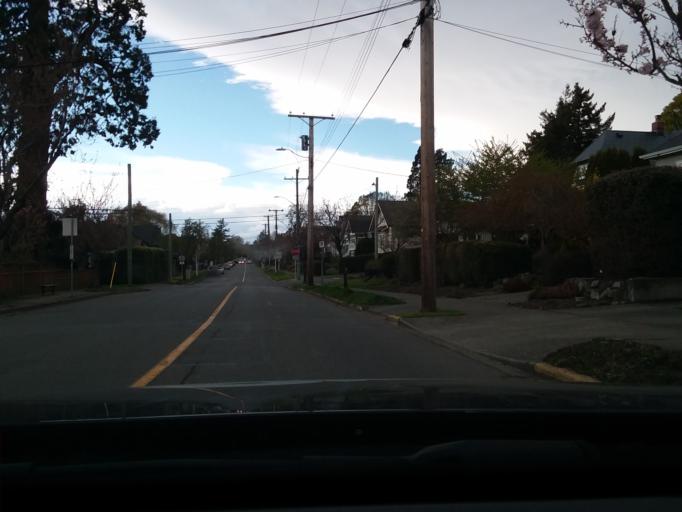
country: CA
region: British Columbia
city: Victoria
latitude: 48.4188
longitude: -123.3472
